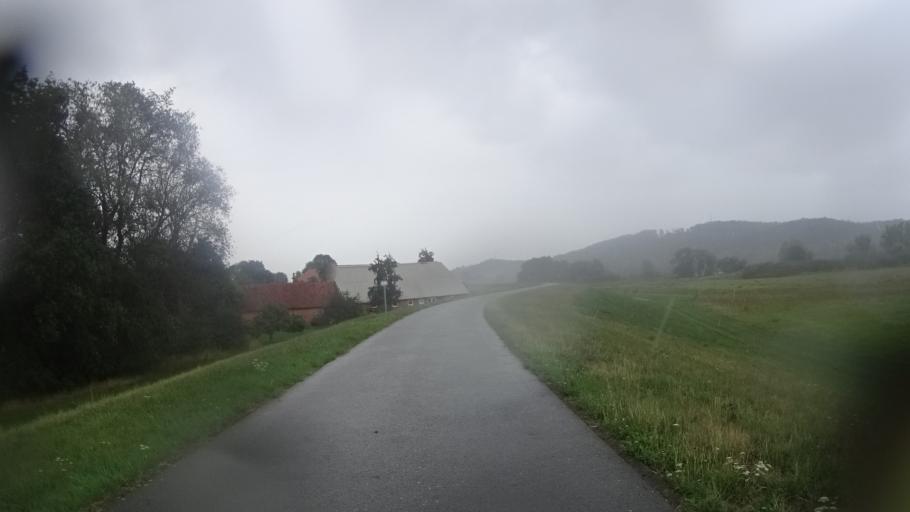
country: DE
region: Lower Saxony
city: Hitzacker
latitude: 53.1698
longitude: 11.0331
